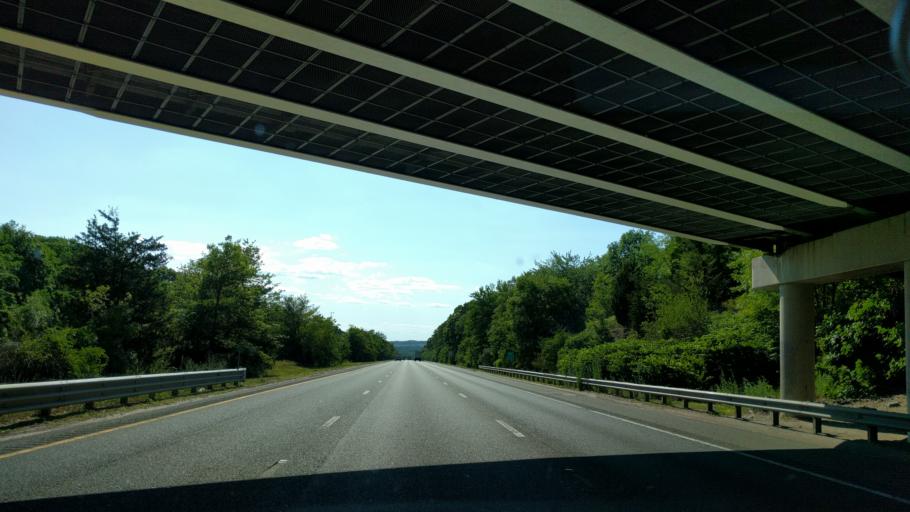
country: US
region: Rhode Island
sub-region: Providence County
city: Valley Falls
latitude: 41.9497
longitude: -71.3538
